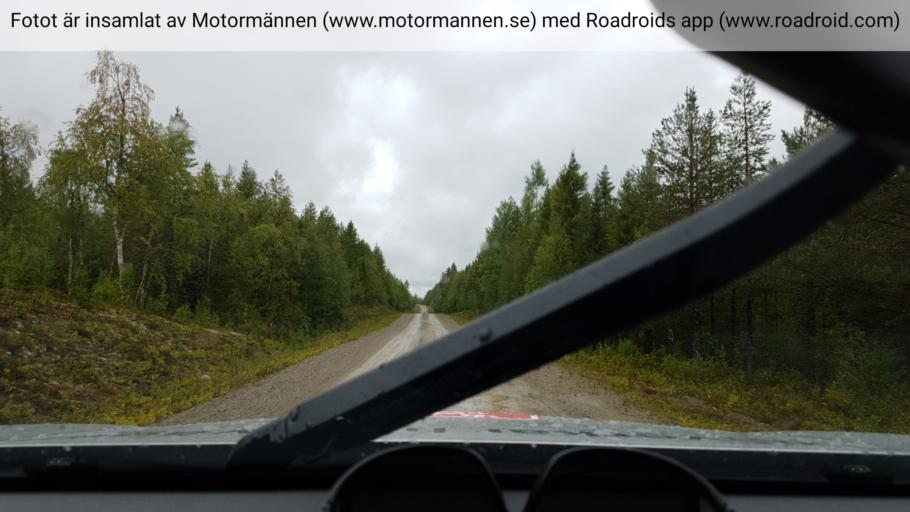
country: SE
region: Vaesterbotten
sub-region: Asele Kommun
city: Insjon
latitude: 64.7884
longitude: 17.6229
